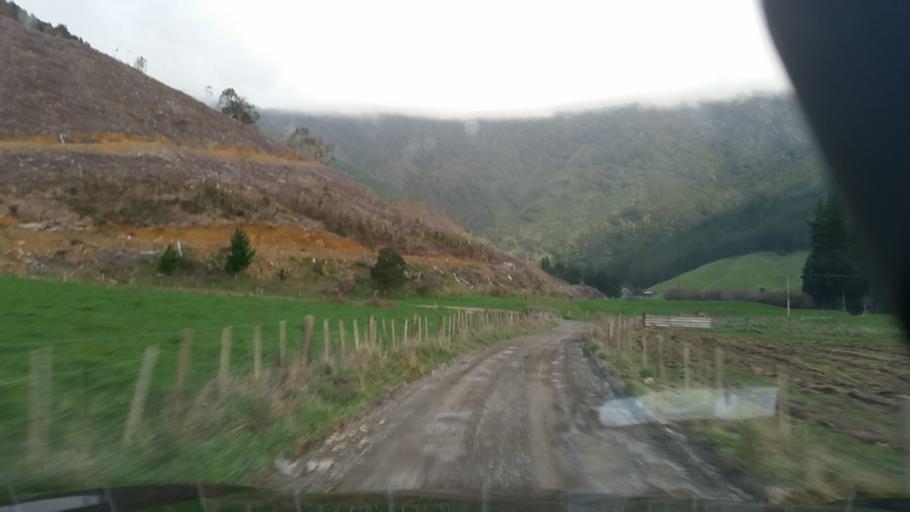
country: NZ
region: Marlborough
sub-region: Marlborough District
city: Picton
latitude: -41.2109
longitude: 173.6948
